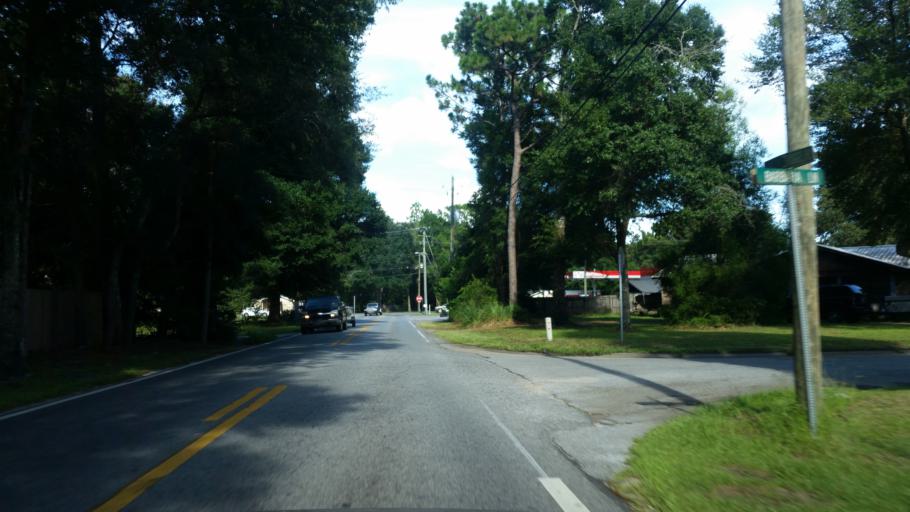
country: US
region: Florida
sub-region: Santa Rosa County
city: Milton
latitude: 30.6203
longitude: -87.0658
